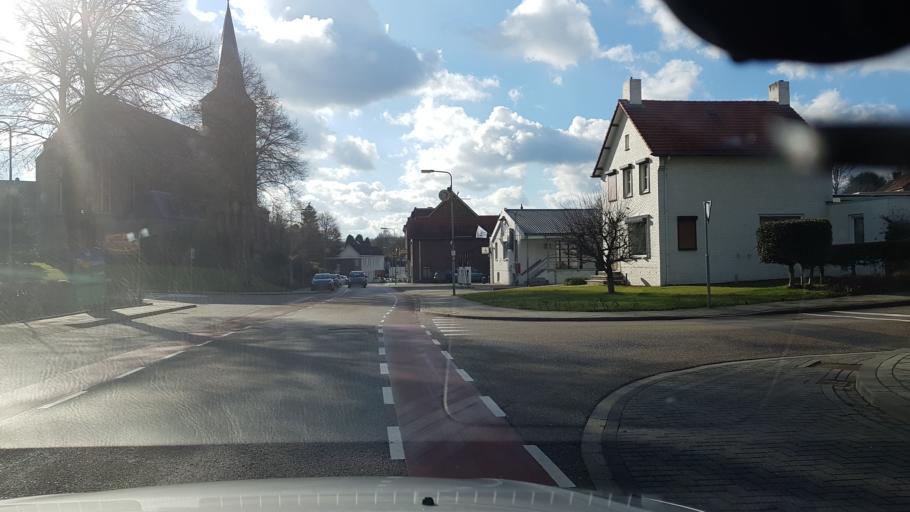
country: NL
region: Limburg
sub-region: Valkenburg aan de Geul
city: Houthem
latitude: 50.9069
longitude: 5.7850
